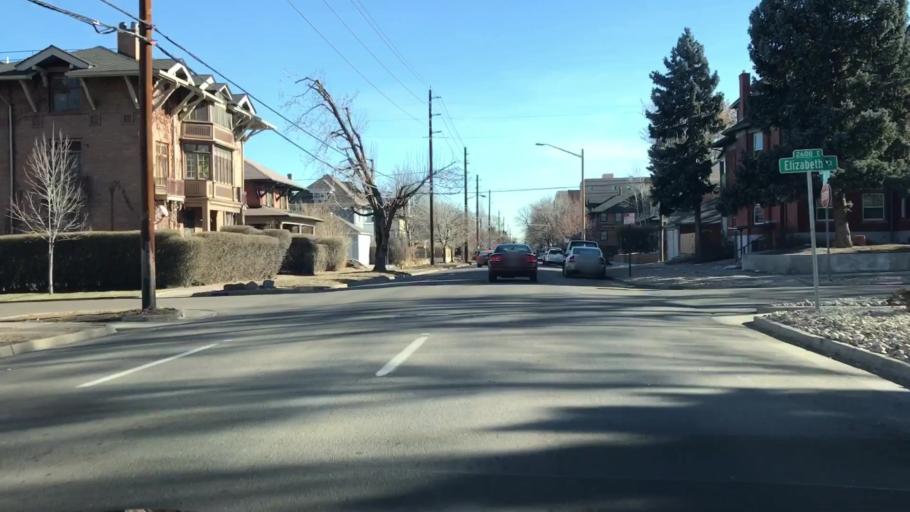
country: US
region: Colorado
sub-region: Denver County
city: Denver
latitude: 39.7383
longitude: -104.9565
